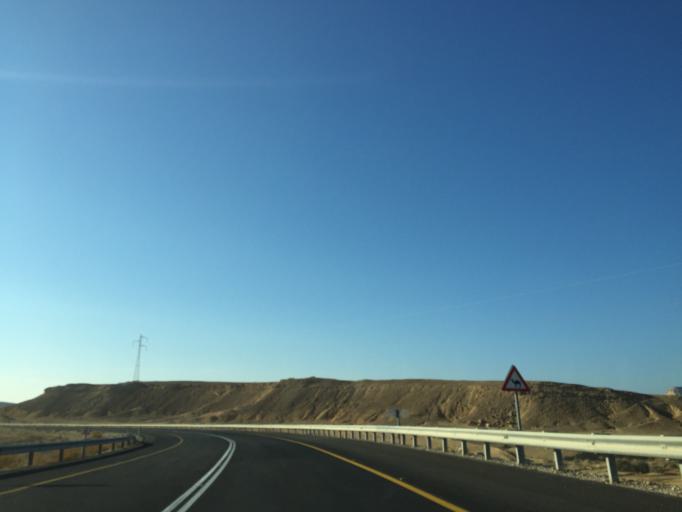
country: IL
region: Southern District
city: Mitzpe Ramon
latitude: 30.3044
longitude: 34.9658
